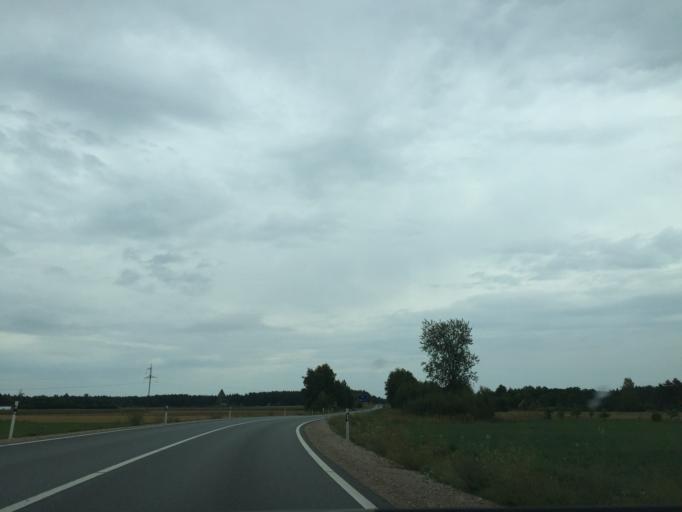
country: LV
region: Jaunpils
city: Jaunpils
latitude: 56.6775
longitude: 23.0893
